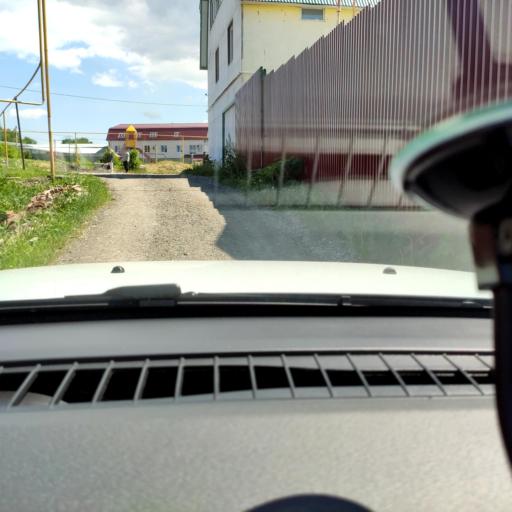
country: RU
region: Samara
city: Samara
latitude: 53.1763
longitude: 50.1623
